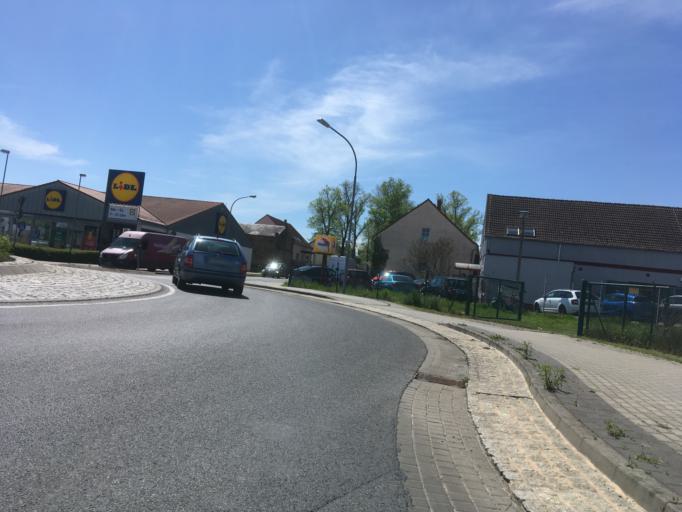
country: DE
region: Brandenburg
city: Wildau
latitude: 52.3233
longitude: 13.6151
